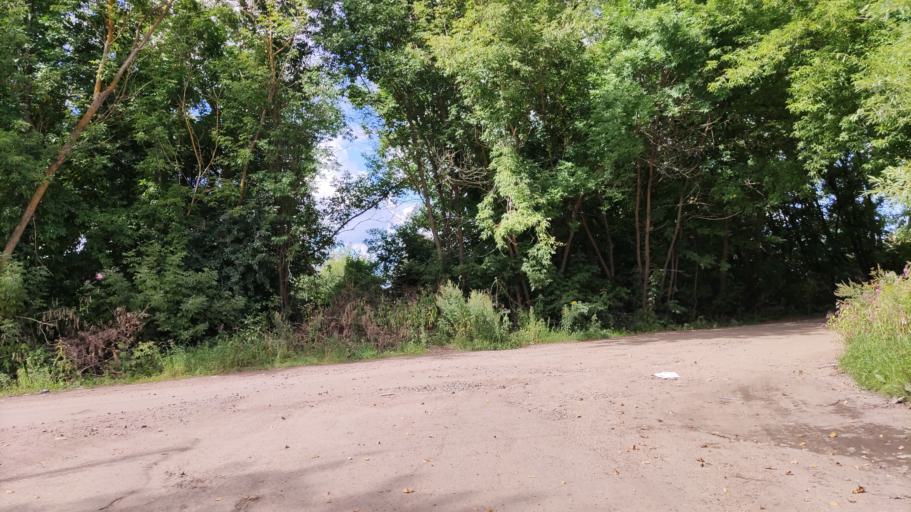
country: RU
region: Tverskaya
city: Rzhev
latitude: 56.2383
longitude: 34.3141
